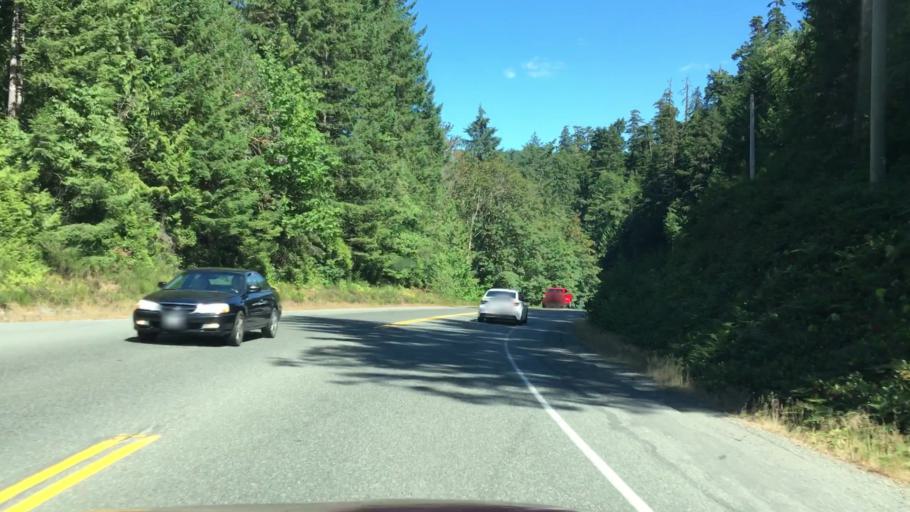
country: CA
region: British Columbia
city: Port Alberni
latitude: 49.2888
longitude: -124.5822
